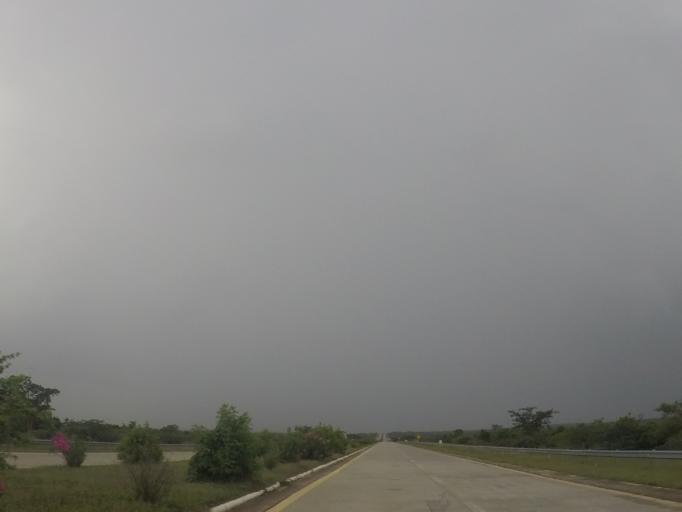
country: MM
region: Mandalay
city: Meiktila
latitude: 21.0319
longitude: 95.7865
